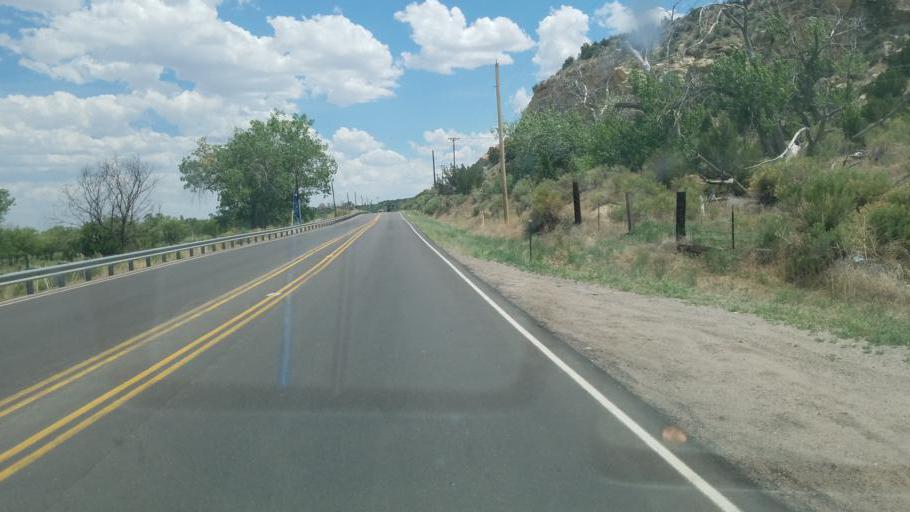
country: US
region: Colorado
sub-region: Fremont County
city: Lincoln Park
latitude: 38.4126
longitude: -105.1761
